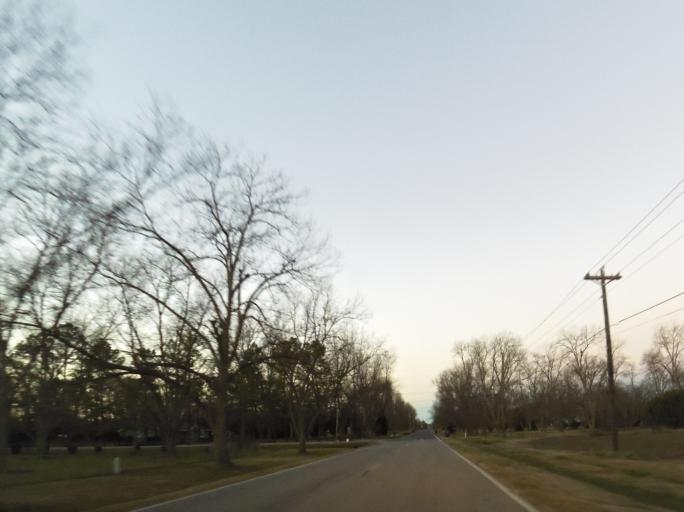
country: US
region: Georgia
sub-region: Peach County
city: Byron
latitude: 32.6180
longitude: -83.7574
